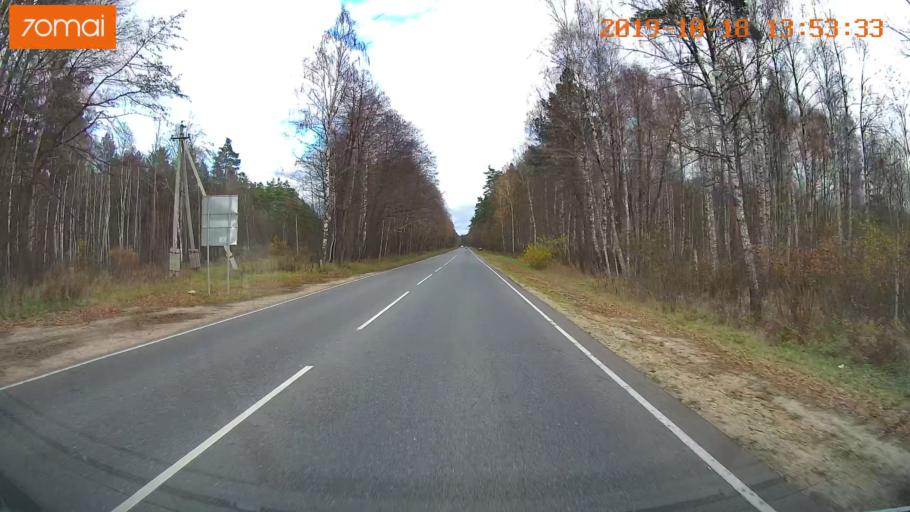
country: RU
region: Moskovskaya
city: Radovitskiy
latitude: 55.0387
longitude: 39.9854
